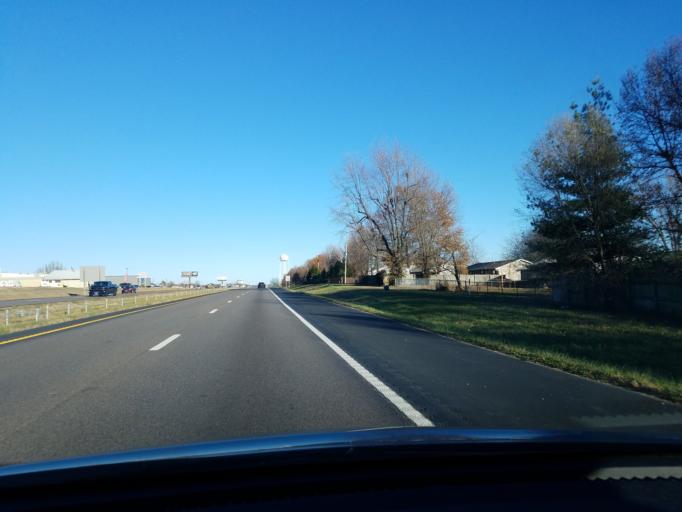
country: US
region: Missouri
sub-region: Phelps County
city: Saint James
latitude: 38.0080
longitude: -91.6120
